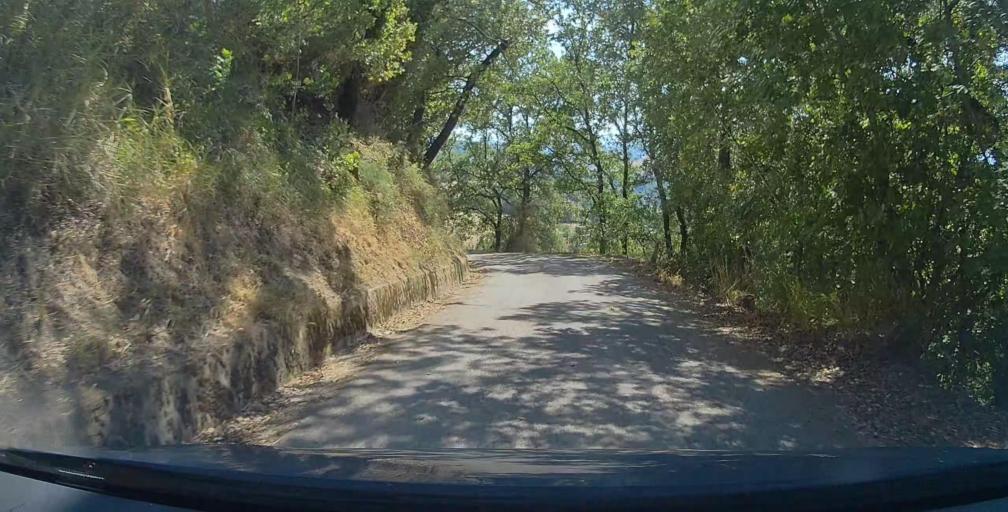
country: IT
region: Latium
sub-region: Provincia di Rieti
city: Collevecchio
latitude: 42.3680
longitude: 12.5583
